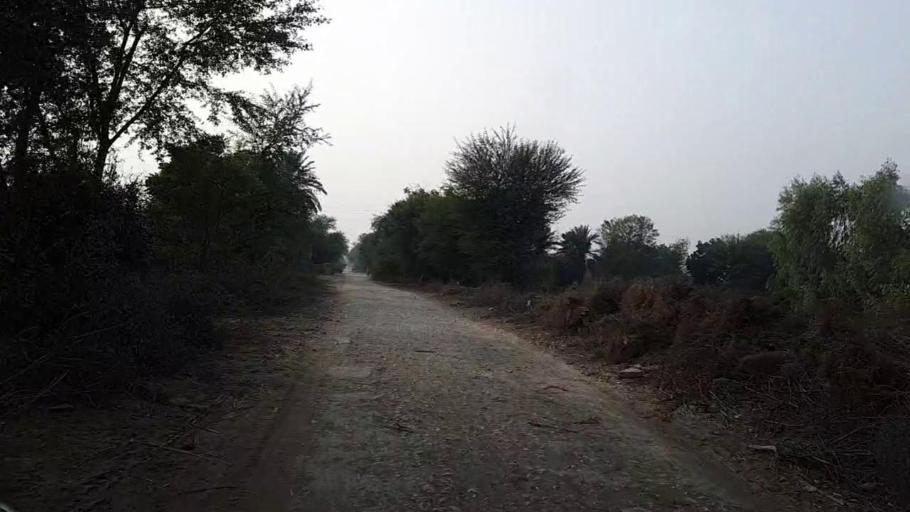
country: PK
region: Sindh
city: Setharja Old
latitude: 27.0809
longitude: 68.5207
